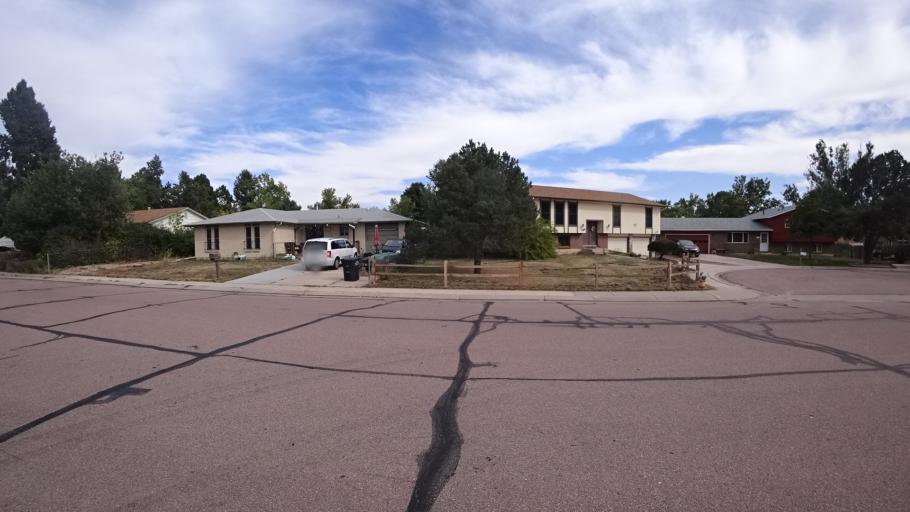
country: US
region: Colorado
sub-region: El Paso County
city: Colorado Springs
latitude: 38.9010
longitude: -104.7753
